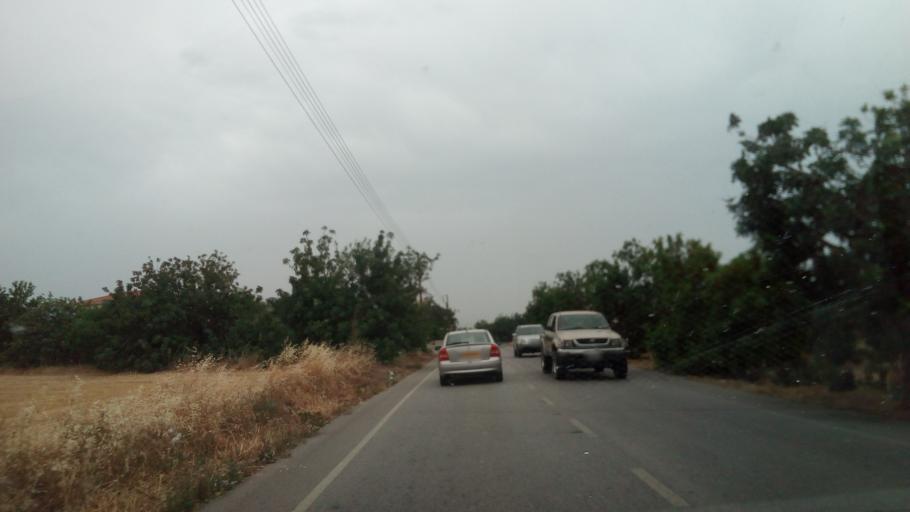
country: CY
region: Pafos
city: Mesogi
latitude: 34.8076
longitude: 32.4500
